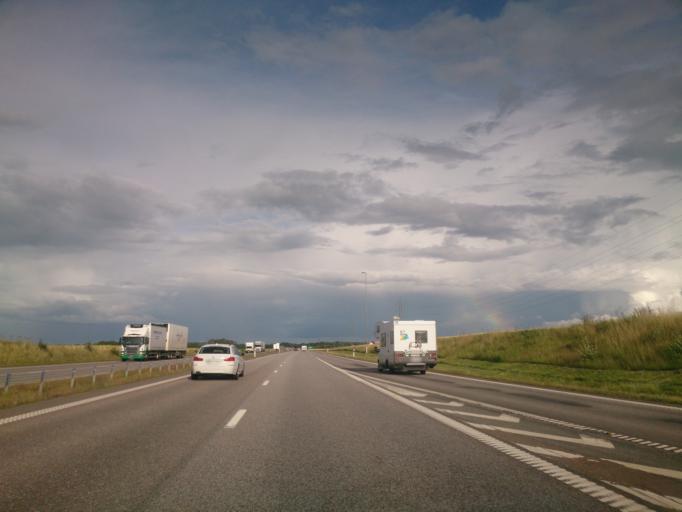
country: SE
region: OEstergoetland
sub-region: Linkopings Kommun
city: Linkoping
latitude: 58.4376
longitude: 15.5884
